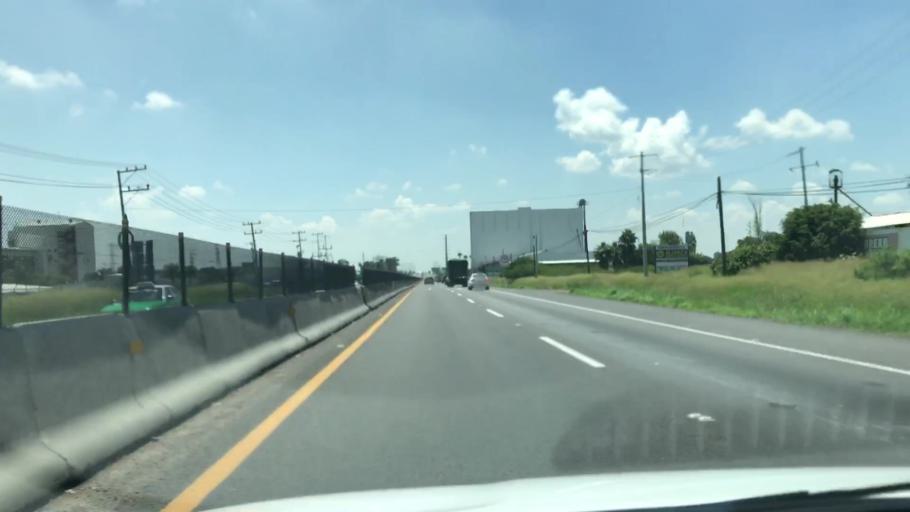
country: MX
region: Guanajuato
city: Villagran
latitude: 20.5092
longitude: -100.9825
